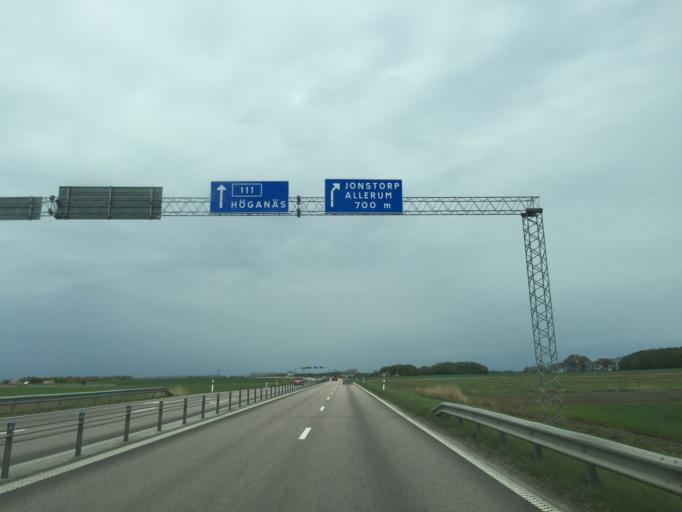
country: SE
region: Skane
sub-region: Helsingborg
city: Odakra
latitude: 56.0880
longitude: 12.7099
